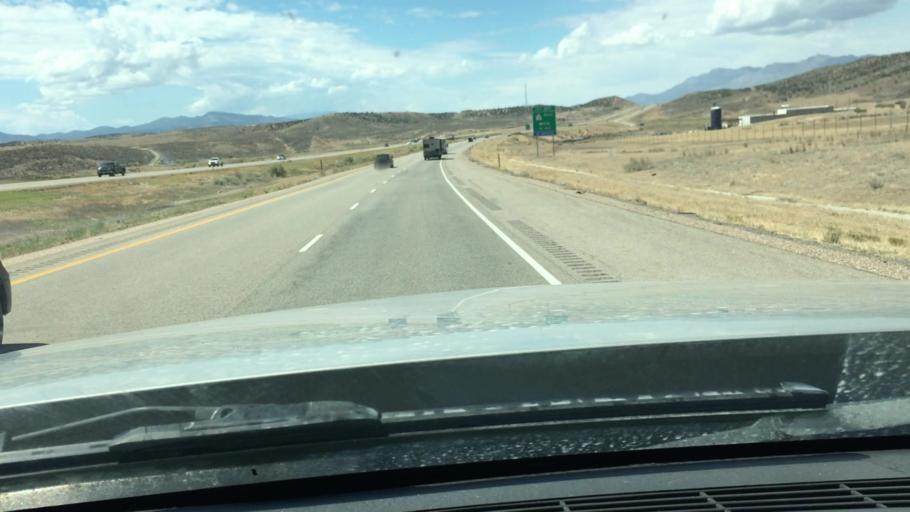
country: US
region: Utah
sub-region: Juab County
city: Nephi
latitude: 39.4935
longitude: -111.9716
